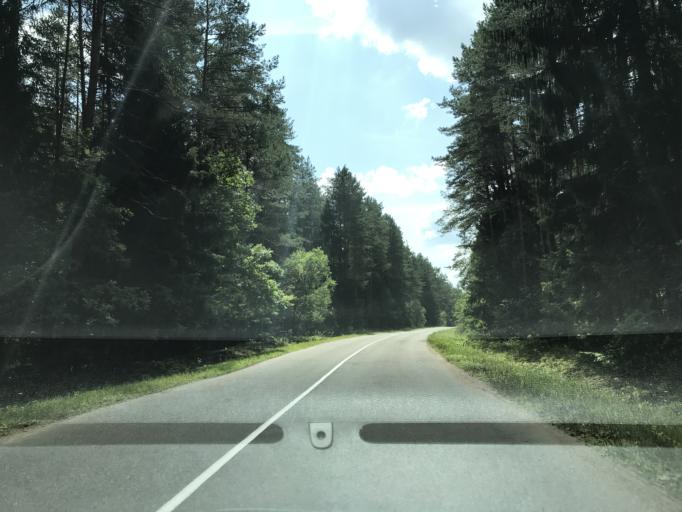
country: BY
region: Minsk
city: Rakaw
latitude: 53.9921
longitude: 26.9912
